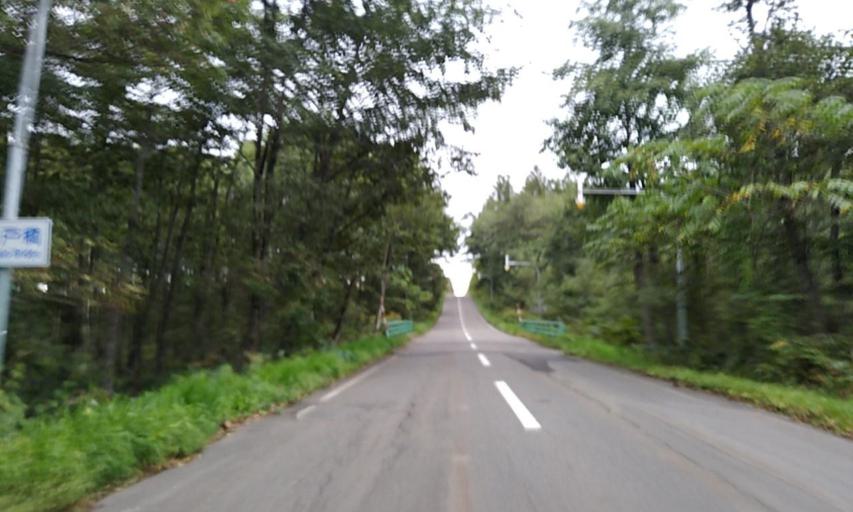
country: JP
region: Hokkaido
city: Obihiro
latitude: 42.6685
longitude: 143.0597
